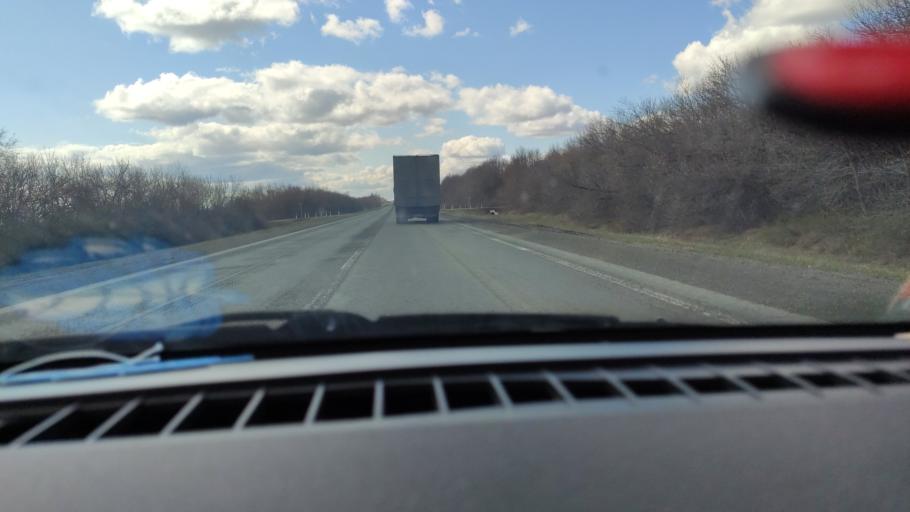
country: RU
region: Saratov
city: Dukhovnitskoye
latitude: 52.6429
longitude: 48.1934
